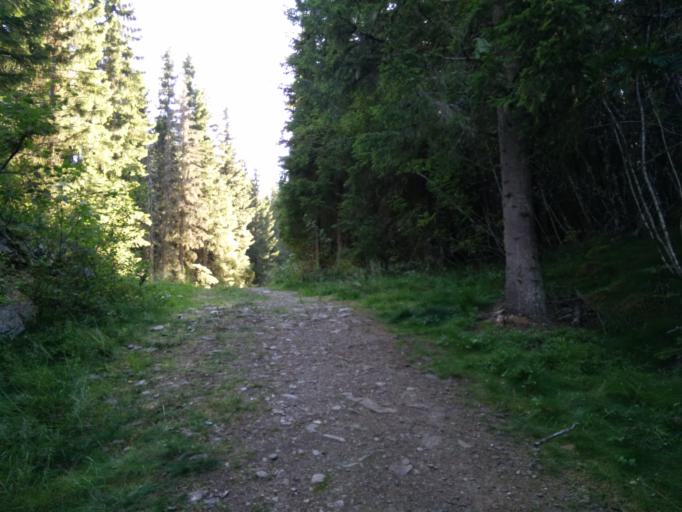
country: NO
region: Sor-Trondelag
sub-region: Skaun
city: Borsa
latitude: 63.3228
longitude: 10.0385
